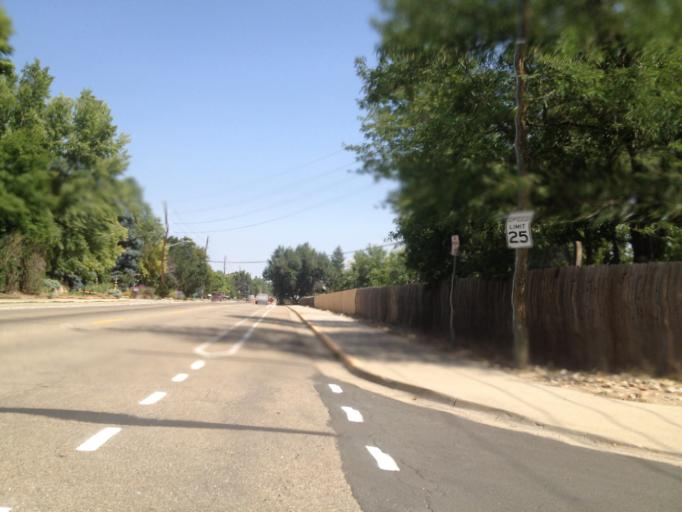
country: US
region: Colorado
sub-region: Boulder County
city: Lafayette
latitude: 39.9941
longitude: -105.1004
